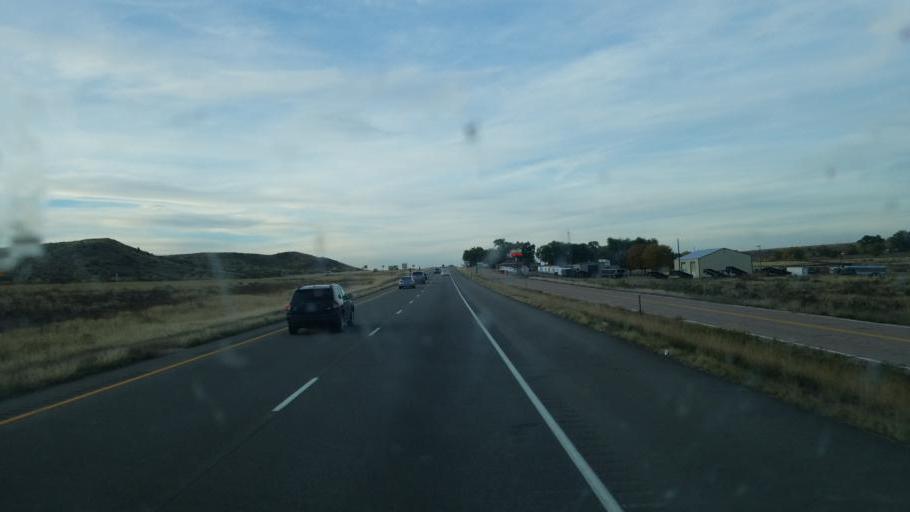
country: US
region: Colorado
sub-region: Pueblo County
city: Pueblo West
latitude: 38.4713
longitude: -104.6133
